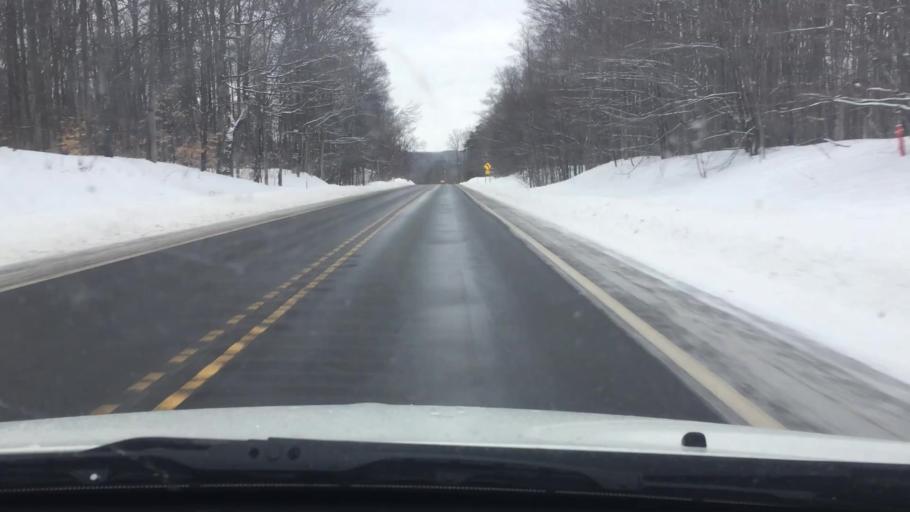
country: US
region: Michigan
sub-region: Charlevoix County
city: East Jordan
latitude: 45.1008
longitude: -85.0286
